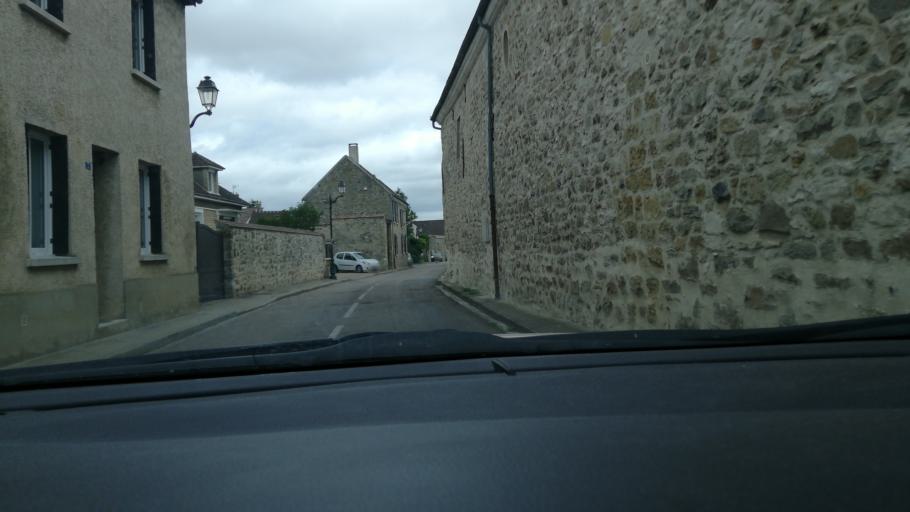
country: FR
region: Ile-de-France
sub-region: Departement du Val-d'Oise
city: Osny
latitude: 49.0898
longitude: 2.0687
